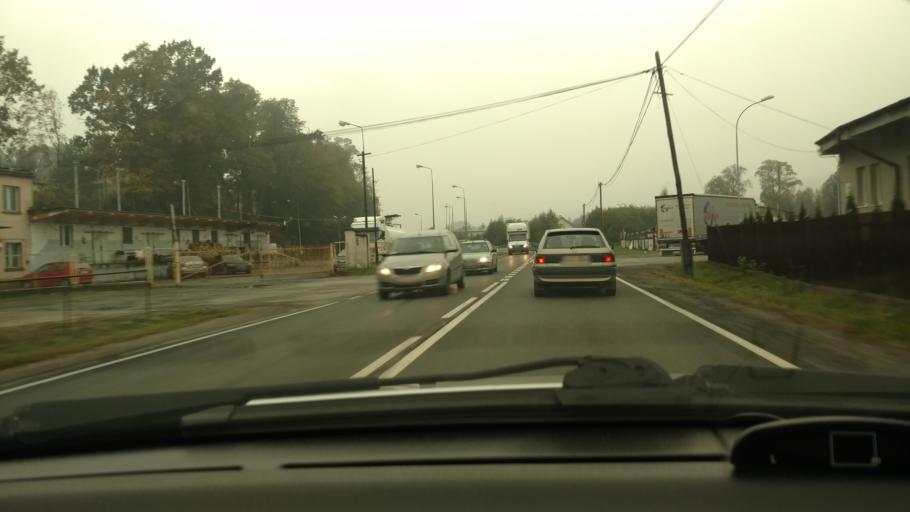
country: PL
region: Lesser Poland Voivodeship
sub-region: Powiat gorlicki
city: Kobylanka
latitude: 49.7043
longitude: 21.2288
